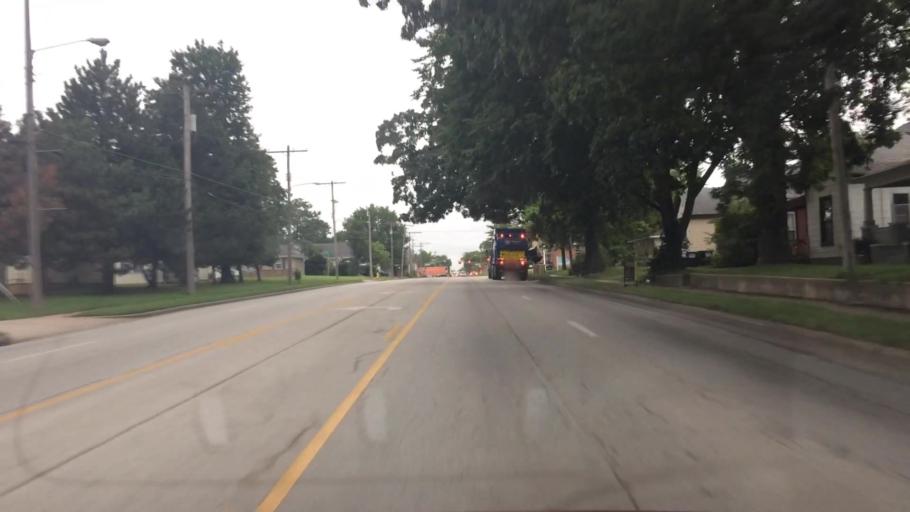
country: US
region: Missouri
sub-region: Greene County
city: Springfield
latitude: 37.2269
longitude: -93.2753
